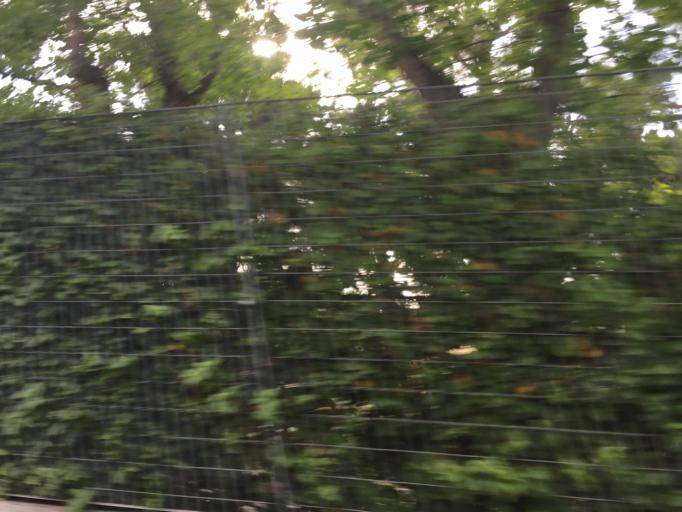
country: IT
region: Apulia
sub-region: Provincia di Bari
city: Triggiano
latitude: 41.0591
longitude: 16.9345
